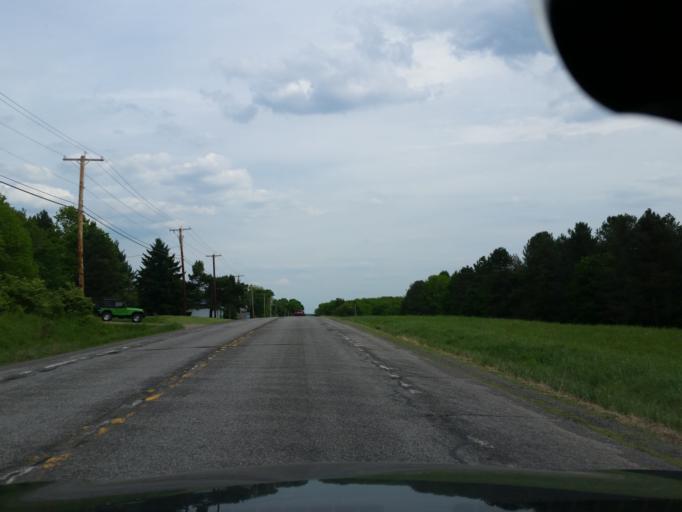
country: US
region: New York
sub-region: Chautauqua County
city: Mayville
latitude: 42.2145
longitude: -79.4287
